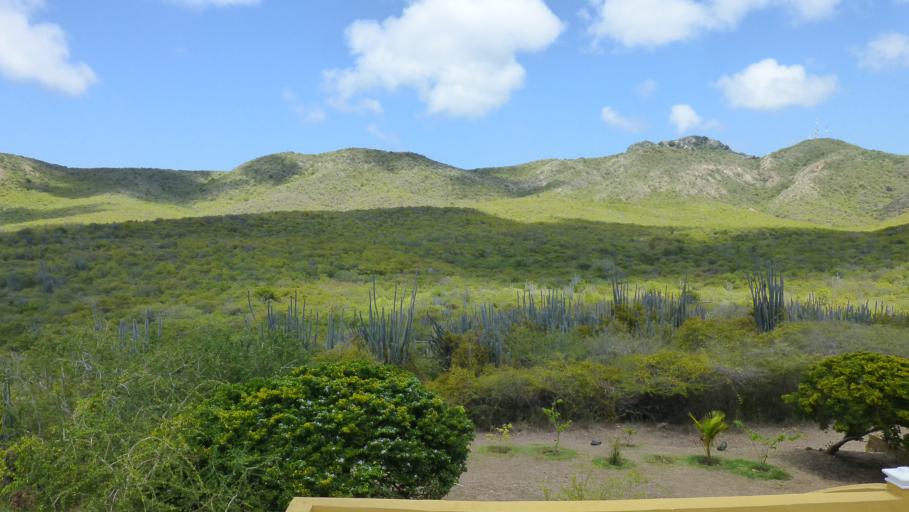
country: CW
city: Dorp Soto
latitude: 12.3445
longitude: -69.1429
